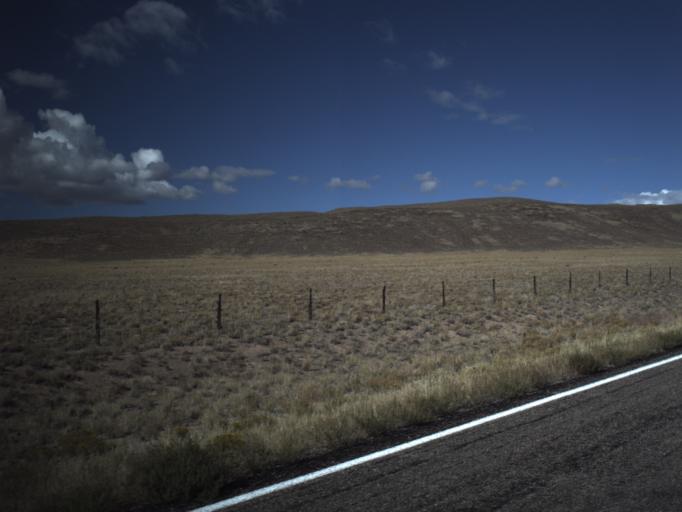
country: US
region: Utah
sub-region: Beaver County
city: Milford
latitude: 38.5975
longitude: -113.8275
